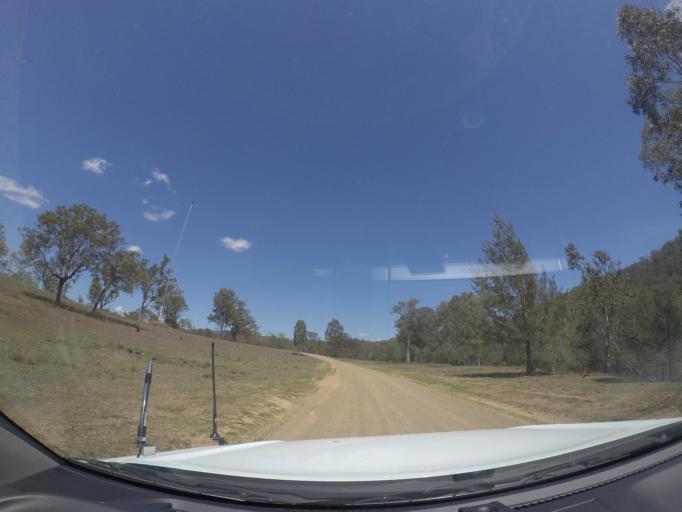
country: AU
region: Queensland
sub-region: Logan
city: Cedar Vale
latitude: -27.8573
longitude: 152.8626
